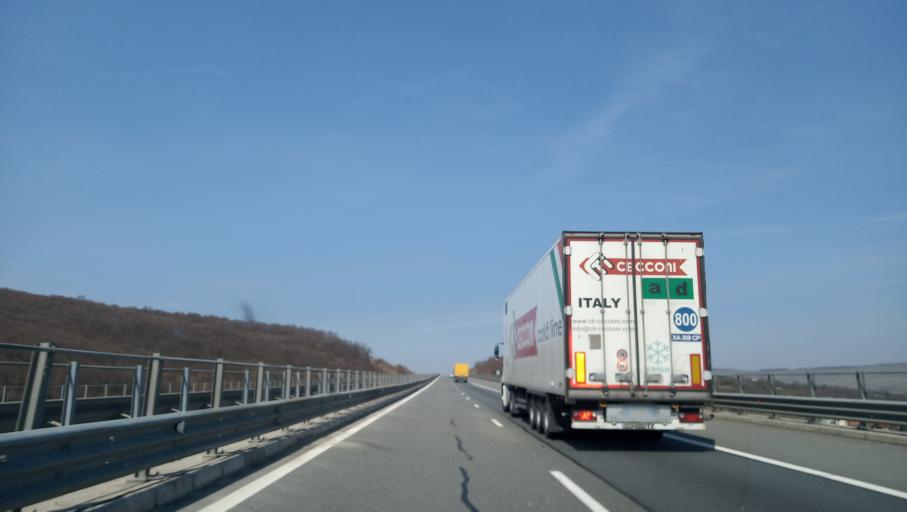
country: RO
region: Cluj
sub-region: Comuna Floresti
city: Luna de Sus
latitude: 46.7325
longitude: 23.4184
